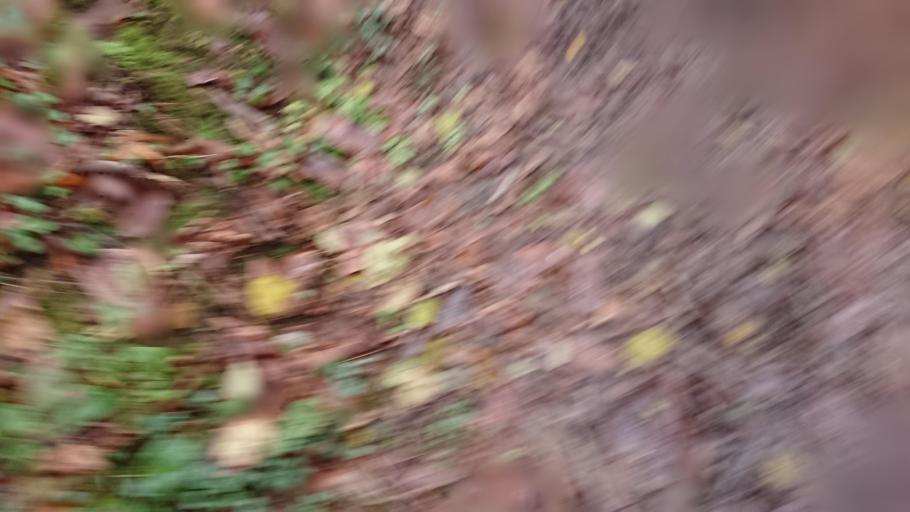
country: GB
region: England
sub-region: Cornwall
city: Fowey
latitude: 50.3360
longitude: -4.5775
